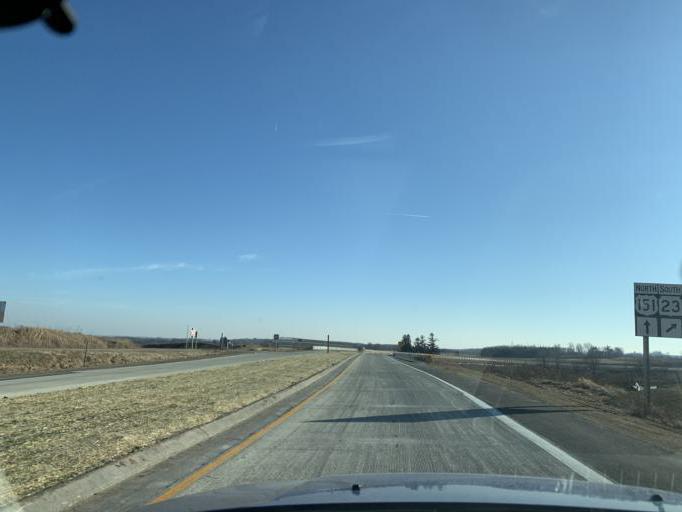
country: US
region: Wisconsin
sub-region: Iowa County
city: Dodgeville
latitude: 42.9382
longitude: -90.1323
